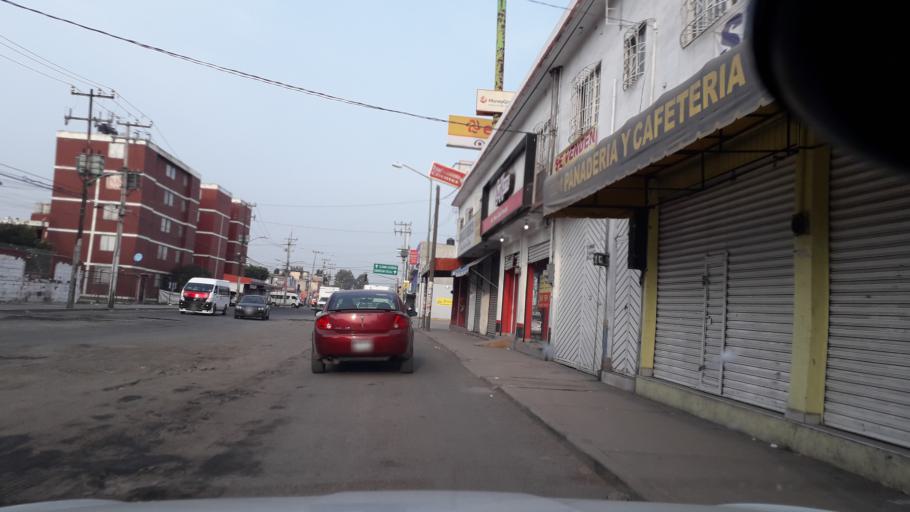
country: MX
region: Mexico
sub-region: Jaltenco
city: Alborada Jaltenco
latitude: 19.6591
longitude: -99.0821
